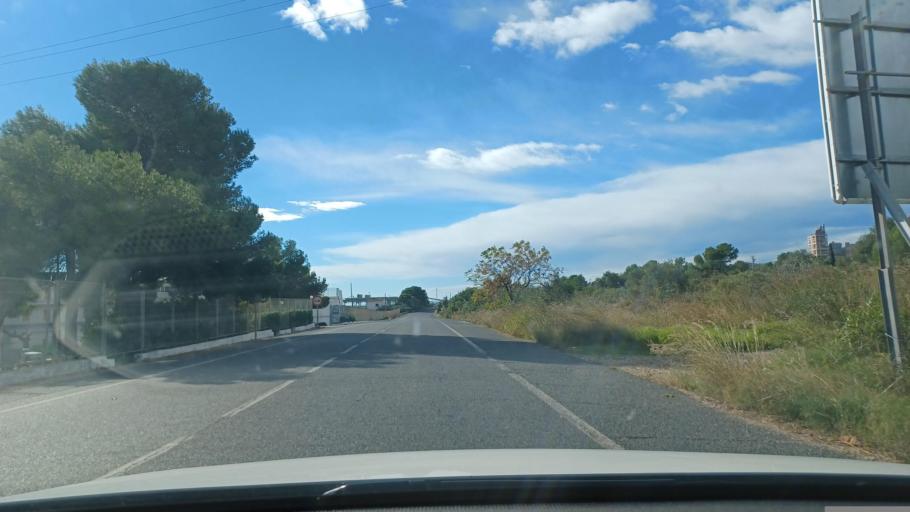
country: ES
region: Catalonia
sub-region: Provincia de Tarragona
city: Sant Carles de la Rapita
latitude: 40.5834
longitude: 0.5562
